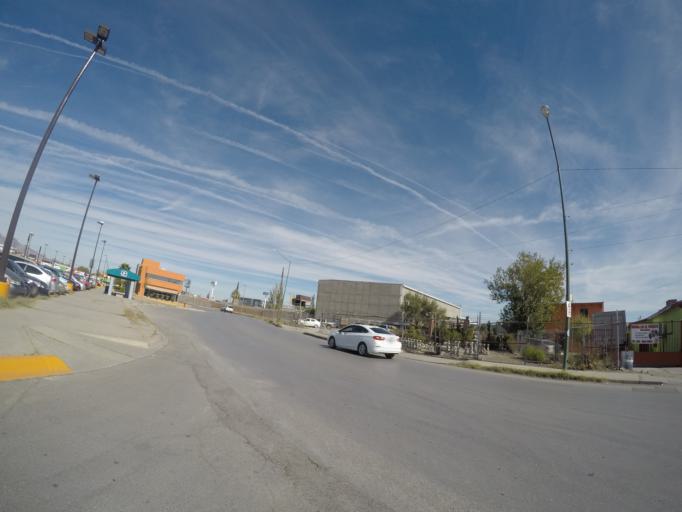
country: MX
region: Chihuahua
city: Ciudad Juarez
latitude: 31.7344
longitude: -106.4453
